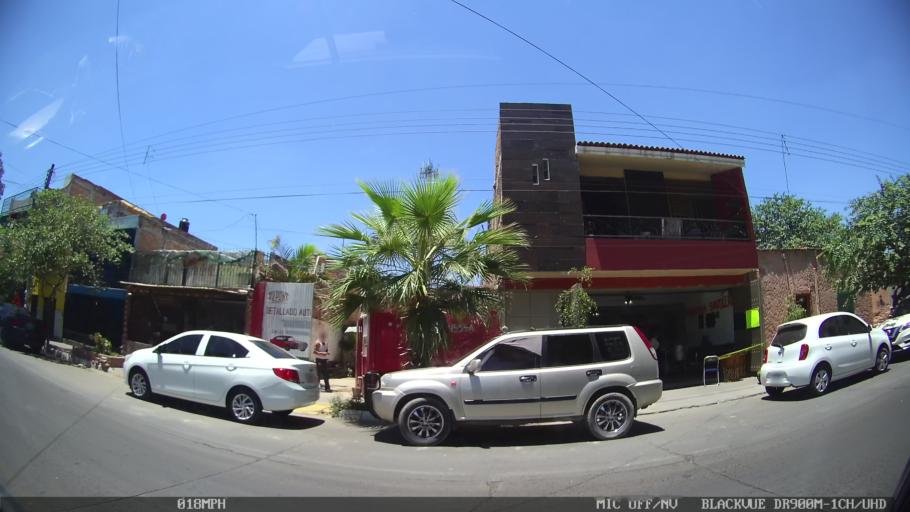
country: MX
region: Jalisco
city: Tlaquepaque
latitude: 20.6595
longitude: -103.2731
